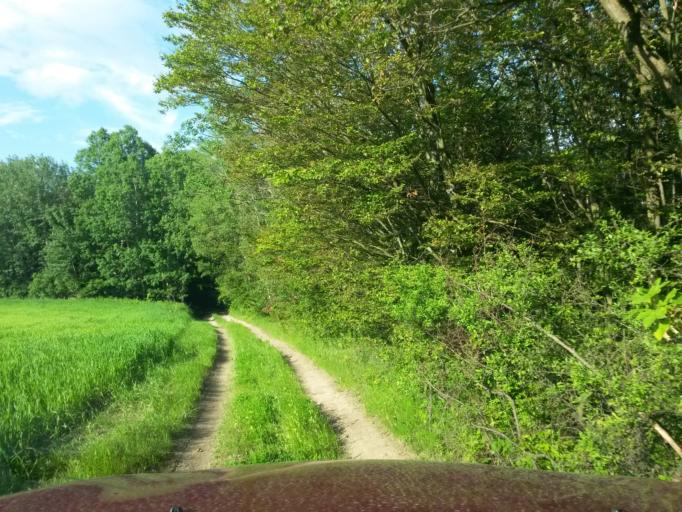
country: SK
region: Kosicky
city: Moldava nad Bodvou
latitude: 48.7268
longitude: 21.0844
